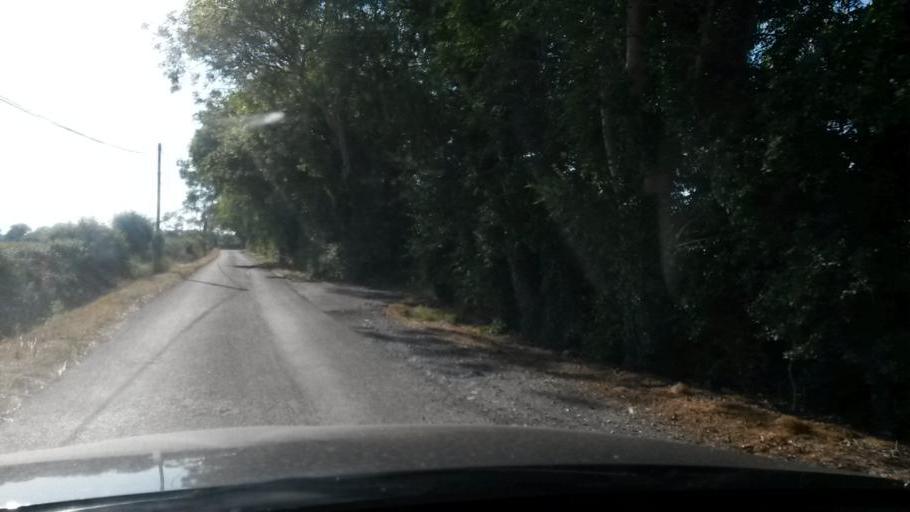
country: IE
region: Leinster
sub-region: Dublin City
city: Finglas
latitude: 53.4316
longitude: -6.3229
